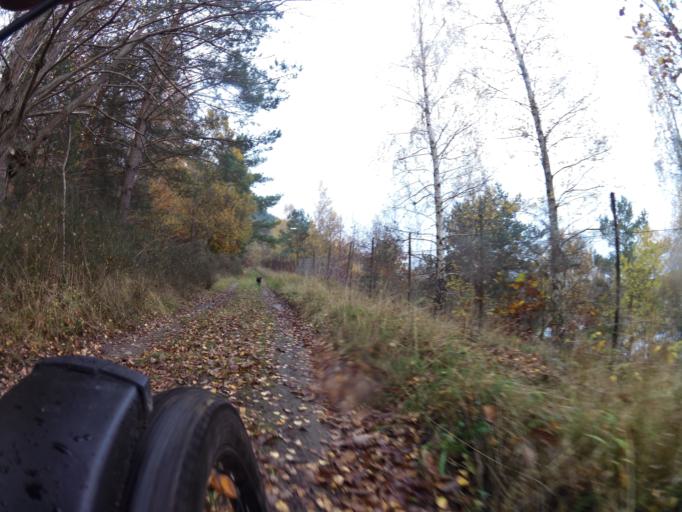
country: PL
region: Pomeranian Voivodeship
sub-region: Powiat wejherowski
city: Gniewino
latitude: 54.7535
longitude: 18.0843
